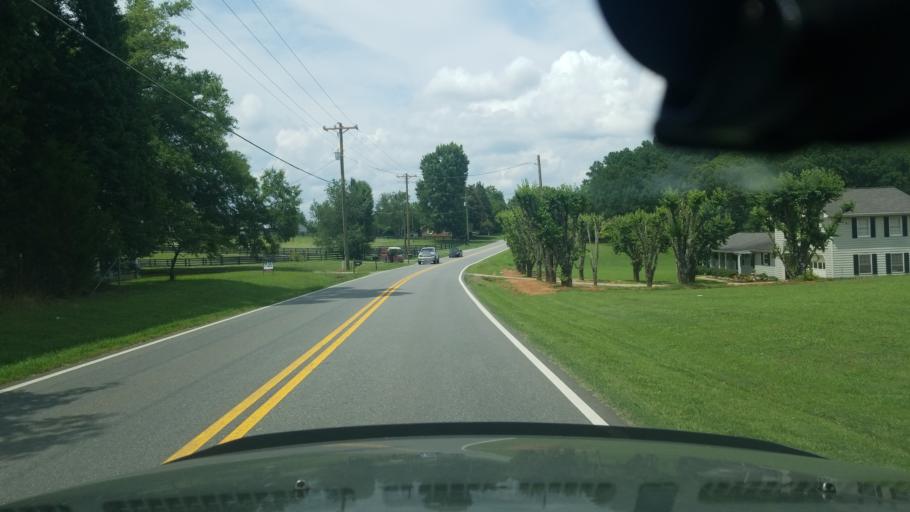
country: US
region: Georgia
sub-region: Forsyth County
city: Cumming
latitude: 34.2617
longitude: -84.2385
